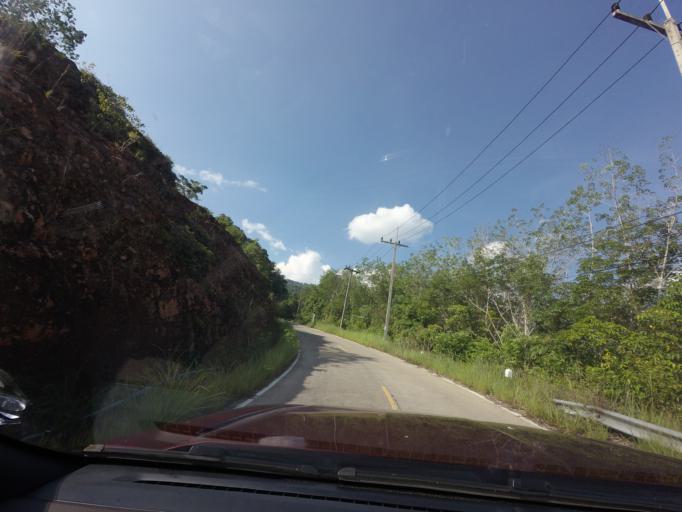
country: TH
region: Yala
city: Than To
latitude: 6.0987
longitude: 101.3109
